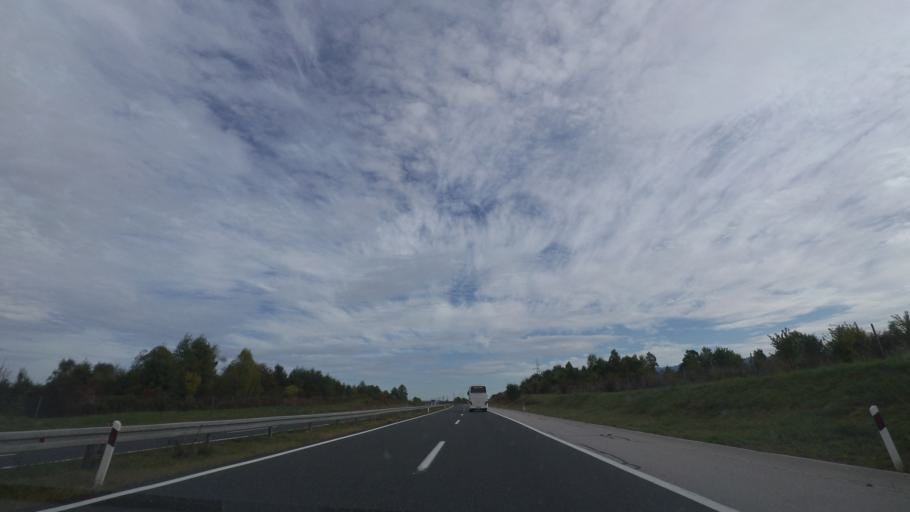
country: HR
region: Licko-Senjska
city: Gospic
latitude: 44.5339
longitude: 15.4440
